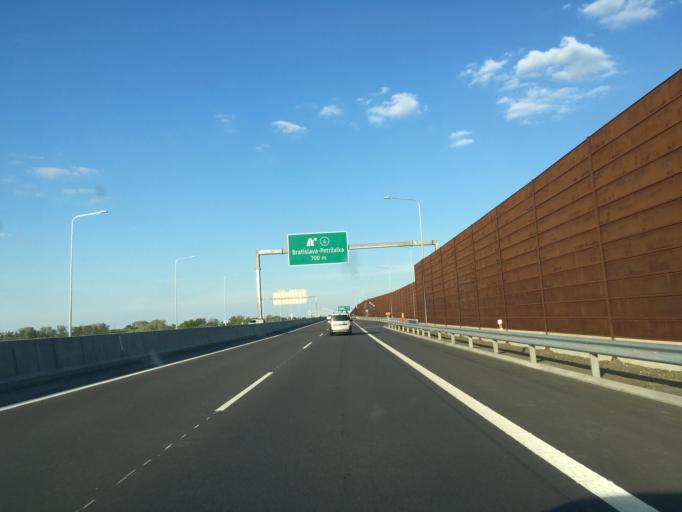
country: AT
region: Burgenland
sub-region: Politischer Bezirk Neusiedl am See
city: Kittsee
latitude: 48.0733
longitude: 17.1162
